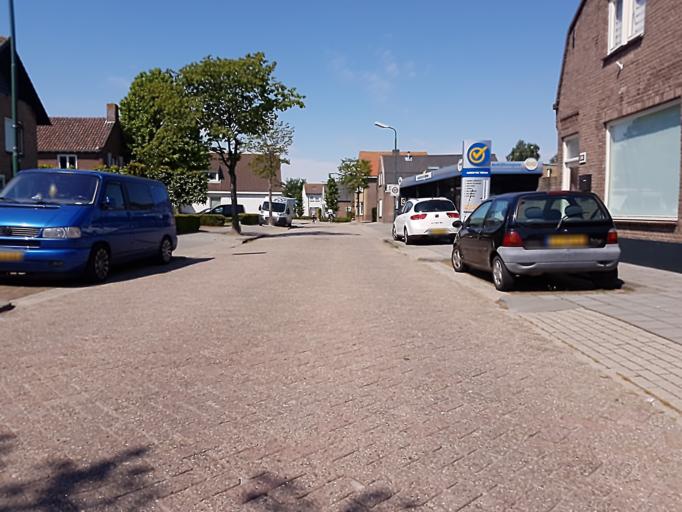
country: NL
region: North Brabant
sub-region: Gemeente Waalwijk
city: Waalwijk
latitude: 51.6627
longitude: 5.0198
